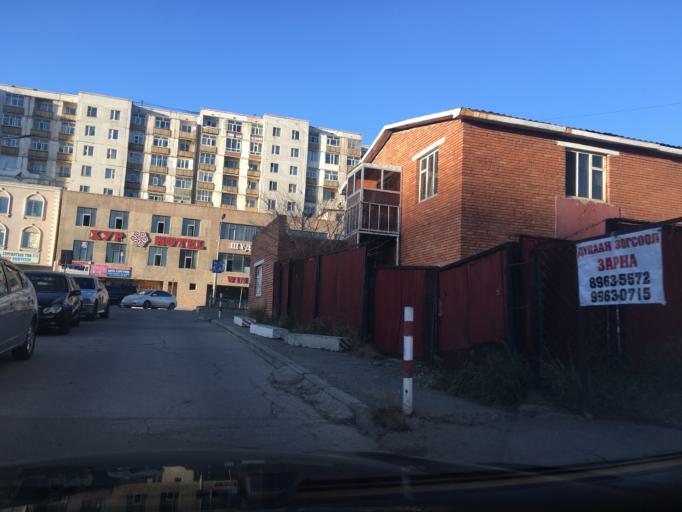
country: MN
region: Ulaanbaatar
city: Ulaanbaatar
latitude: 47.9247
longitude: 106.8793
